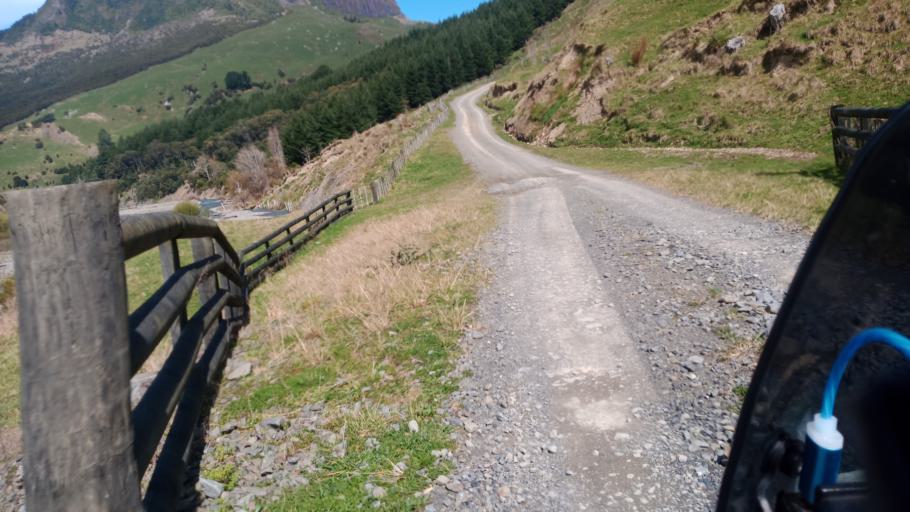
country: NZ
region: Gisborne
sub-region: Gisborne District
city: Gisborne
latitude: -37.8537
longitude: 178.0882
